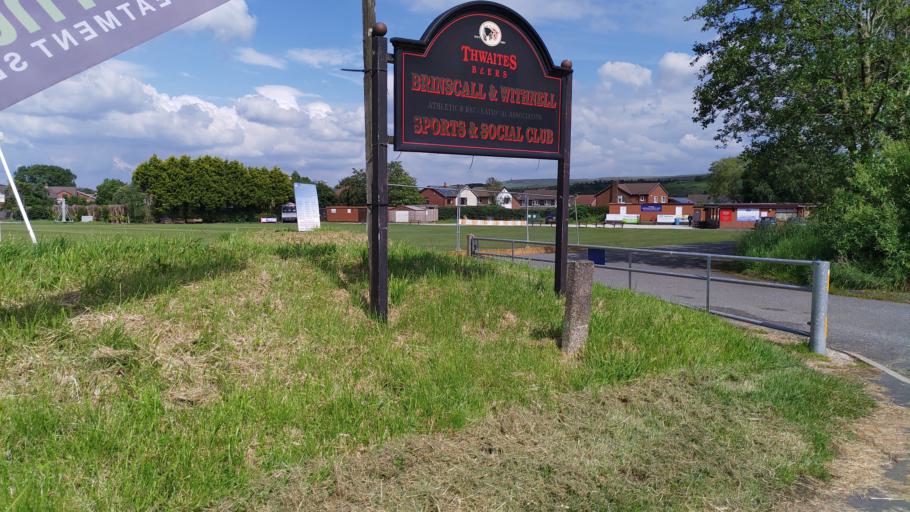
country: GB
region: England
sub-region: Lancashire
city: Chorley
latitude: 53.6895
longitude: -2.5741
